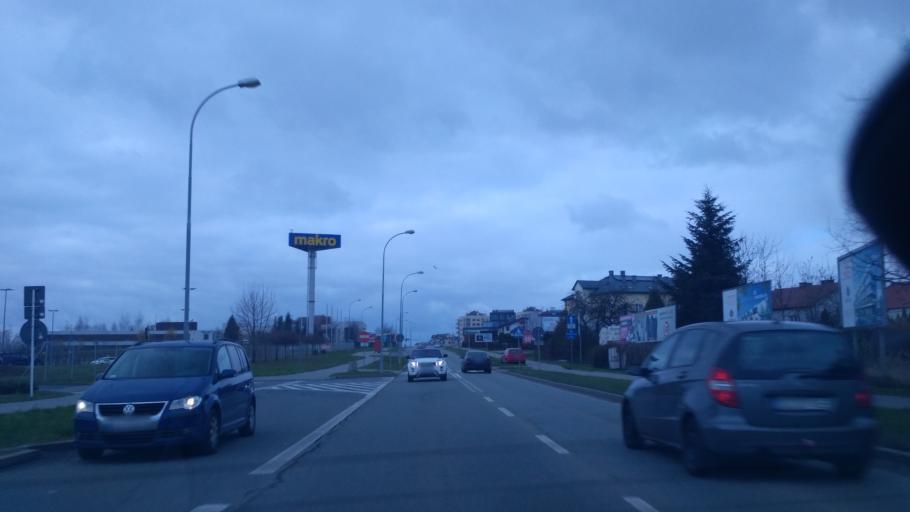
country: PL
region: Subcarpathian Voivodeship
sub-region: Rzeszow
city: Rzeszow
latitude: 50.0319
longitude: 22.0394
